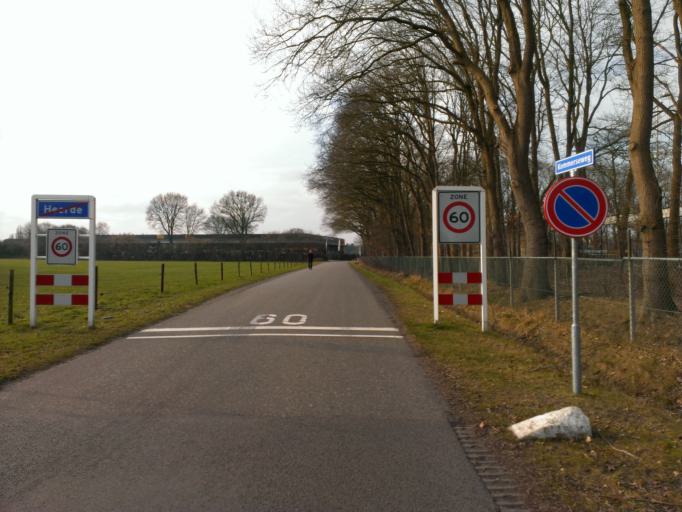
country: NL
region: Gelderland
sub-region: Gemeente Heerde
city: Heerde
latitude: 52.3988
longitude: 6.0411
